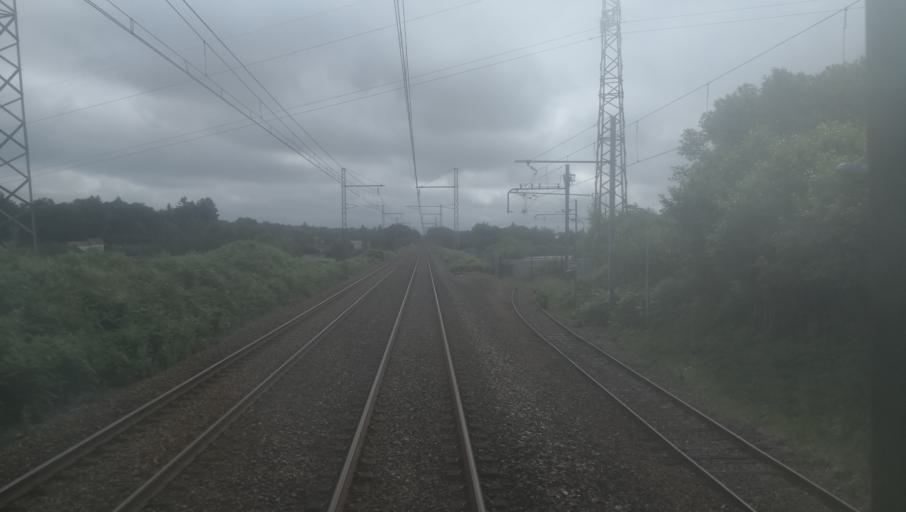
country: FR
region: Limousin
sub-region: Departement de la Haute-Vienne
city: Ambazac
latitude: 45.9562
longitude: 1.4158
